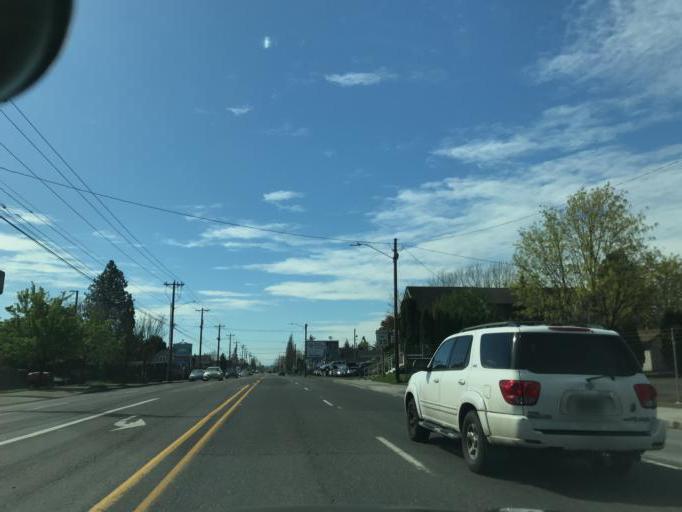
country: US
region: Oregon
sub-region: Multnomah County
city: Lents
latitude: 45.4759
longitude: -122.5791
